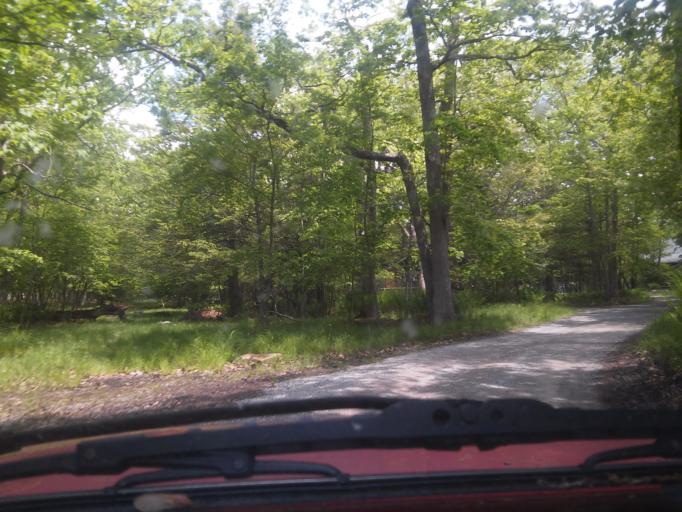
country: US
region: Virginia
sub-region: Giles County
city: Pembroke
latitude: 37.3747
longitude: -80.5233
